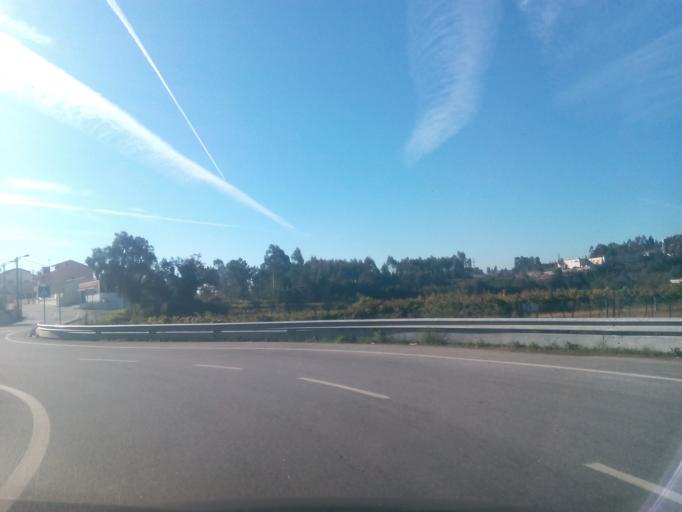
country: PT
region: Porto
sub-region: Paredes
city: Gandra
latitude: 41.2038
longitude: -8.4433
